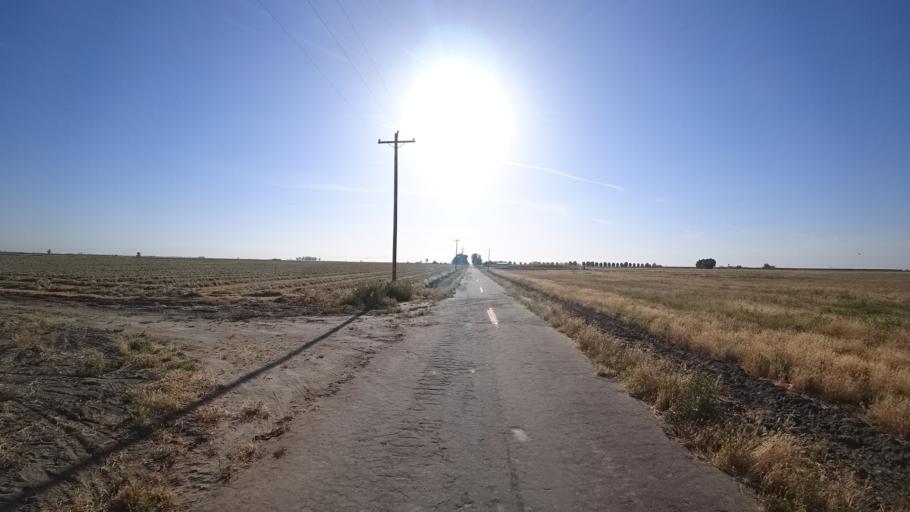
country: US
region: California
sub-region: Kings County
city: Stratford
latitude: 36.1748
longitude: -119.7914
